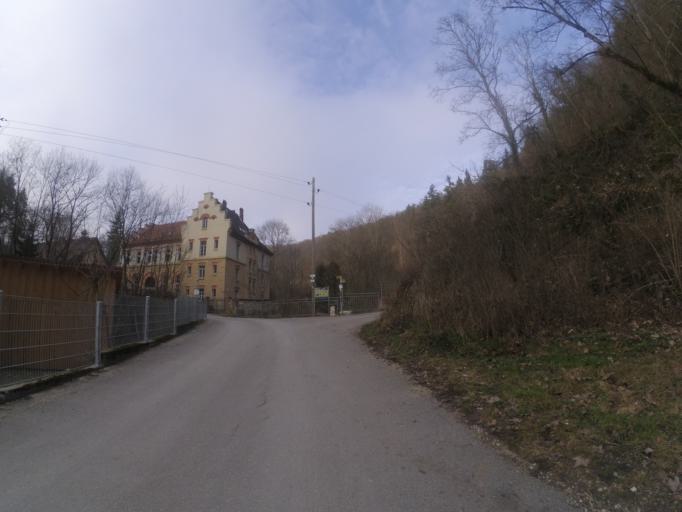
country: DE
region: Baden-Wuerttemberg
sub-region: Tuebingen Region
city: Lauterach
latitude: 48.2608
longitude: 9.5630
